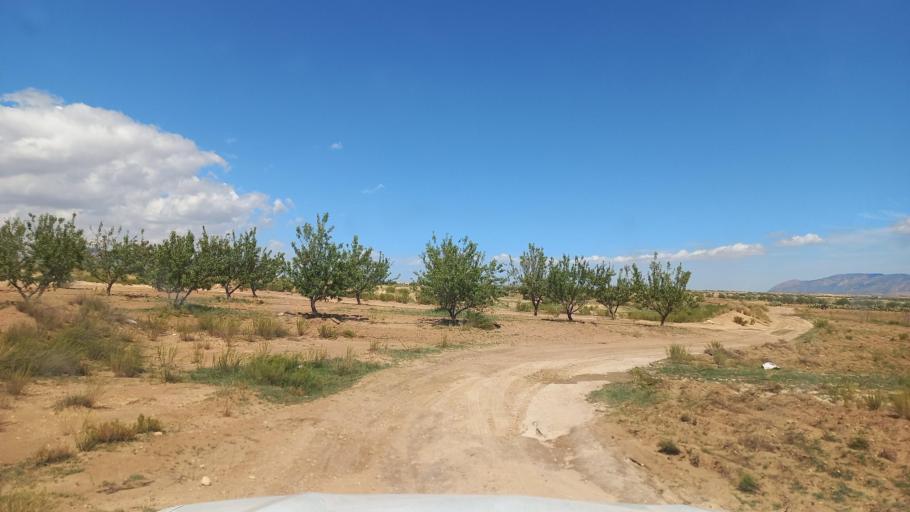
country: TN
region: Al Qasrayn
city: Sbiba
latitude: 35.3510
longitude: 9.0190
